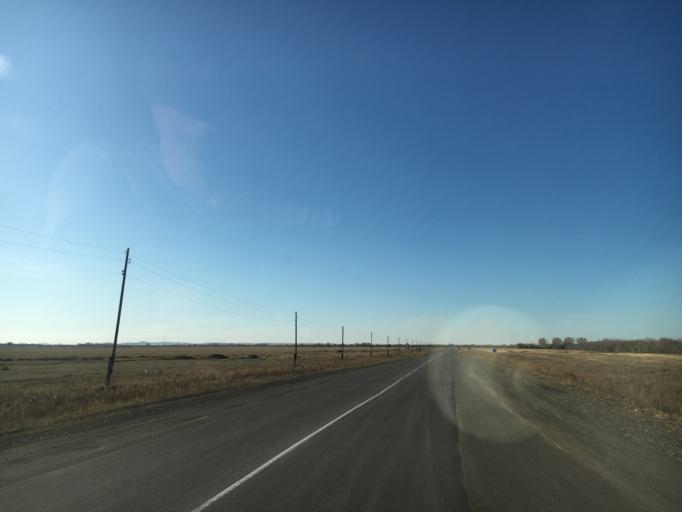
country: KZ
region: Qaraghandy
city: Tokarevka
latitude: 50.1199
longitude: 73.2108
